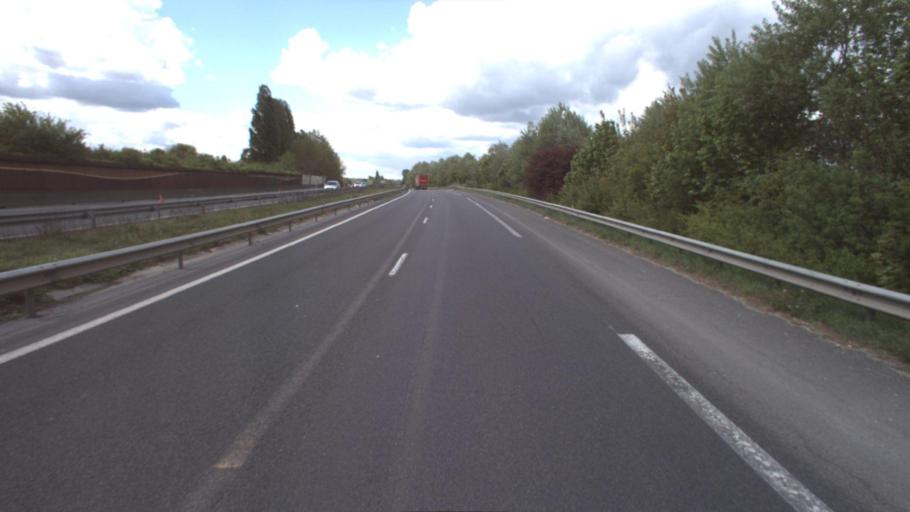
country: FR
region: Ile-de-France
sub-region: Departement de Seine-et-Marne
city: Fontenay-Tresigny
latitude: 48.7123
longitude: 2.8713
